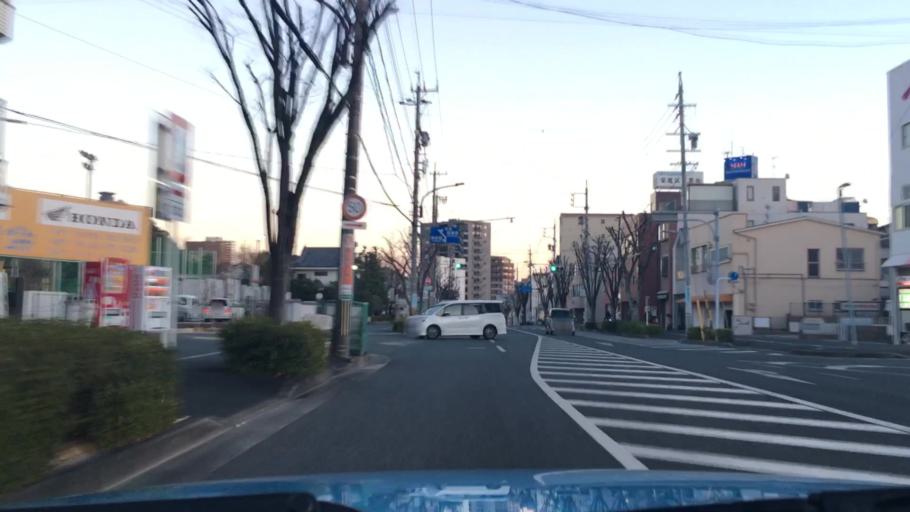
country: JP
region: Shizuoka
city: Hamamatsu
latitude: 34.7128
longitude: 137.7219
